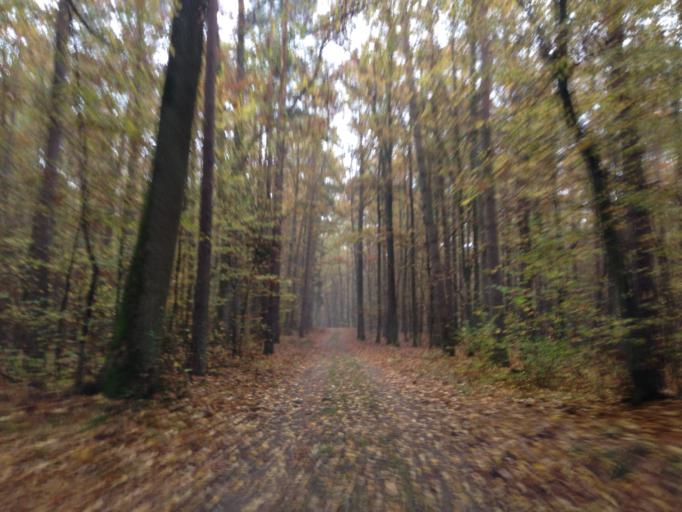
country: PL
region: Kujawsko-Pomorskie
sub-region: Powiat brodnicki
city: Gorzno
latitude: 53.2357
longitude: 19.7291
